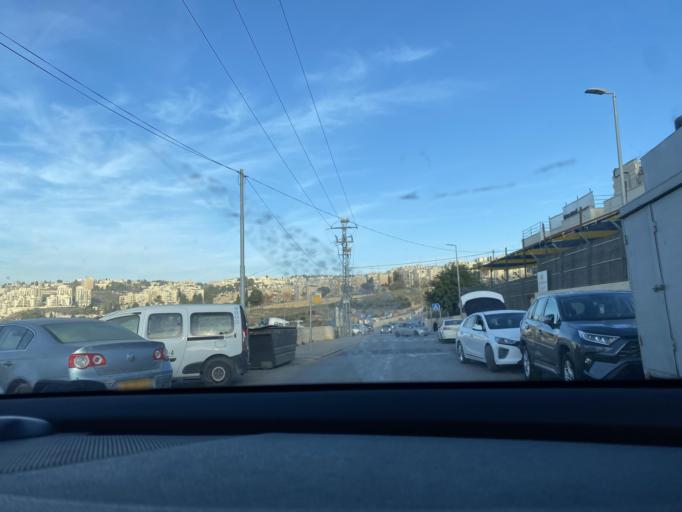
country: PS
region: West Bank
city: Ash Shaykh Sa`d
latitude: 31.7409
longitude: 35.2415
